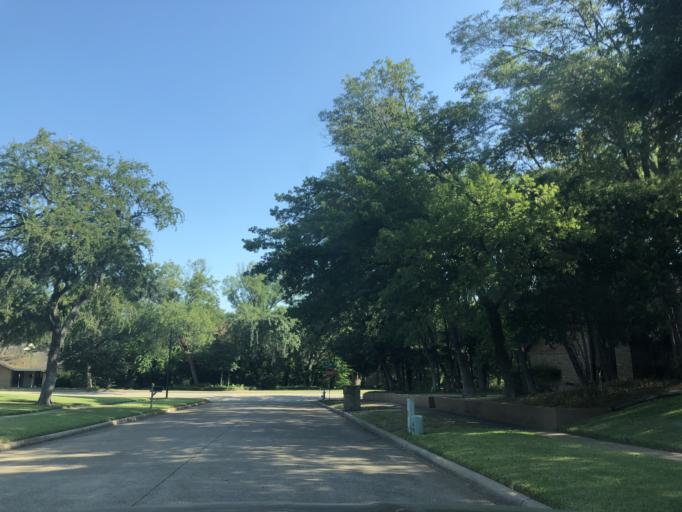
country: US
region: Texas
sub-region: Dallas County
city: Garland
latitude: 32.8703
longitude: -96.6419
